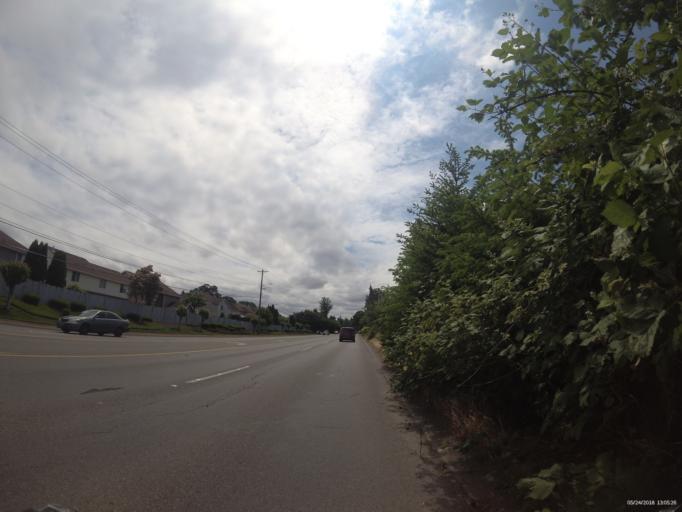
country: US
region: Washington
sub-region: Pierce County
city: Lakewood
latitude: 47.1858
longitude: -122.5087
